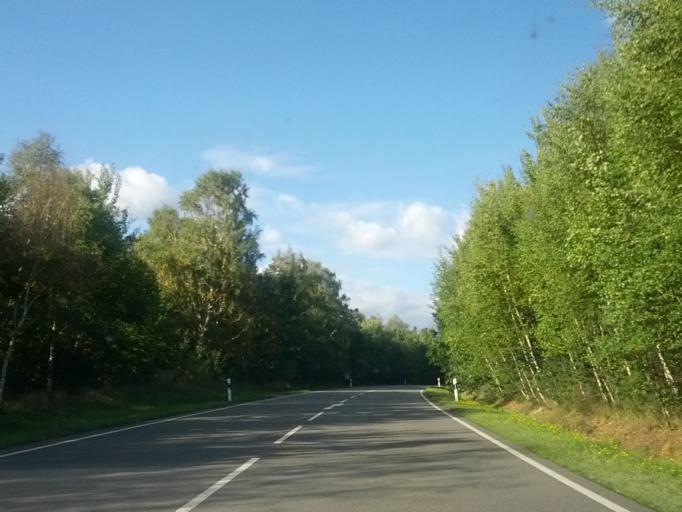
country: DE
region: Thuringia
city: Barchfeld
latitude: 50.7859
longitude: 10.3154
